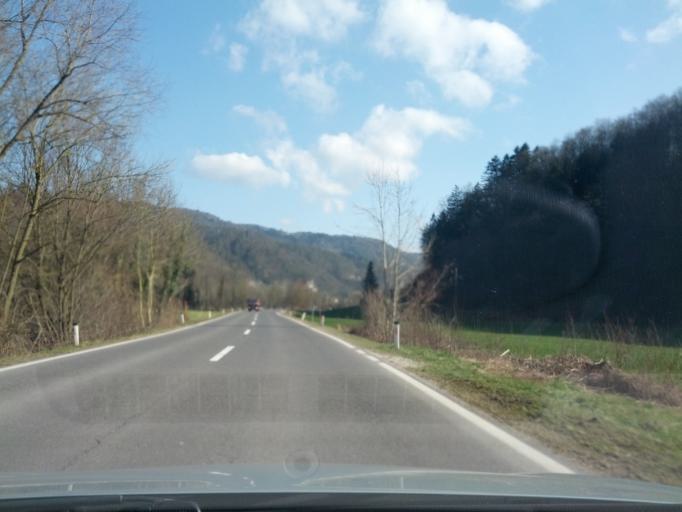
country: SI
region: Smartno pri Litiji
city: Smartno pri Litiji
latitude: 46.0800
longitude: 14.8754
